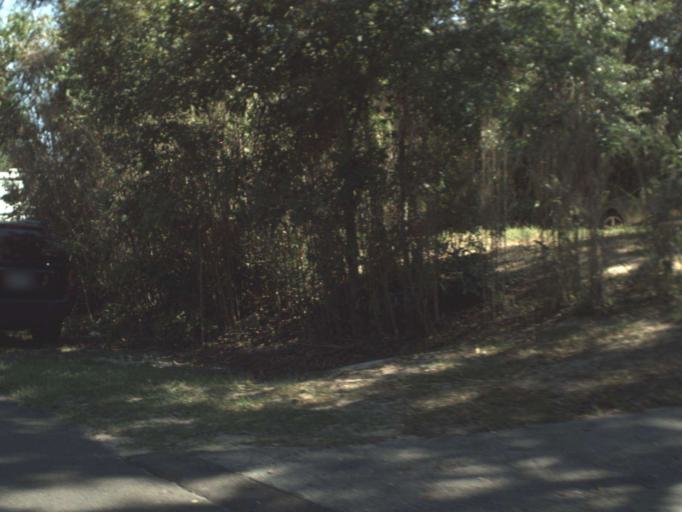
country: US
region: Florida
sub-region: Walton County
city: Miramar Beach
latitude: 30.4653
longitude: -86.3633
